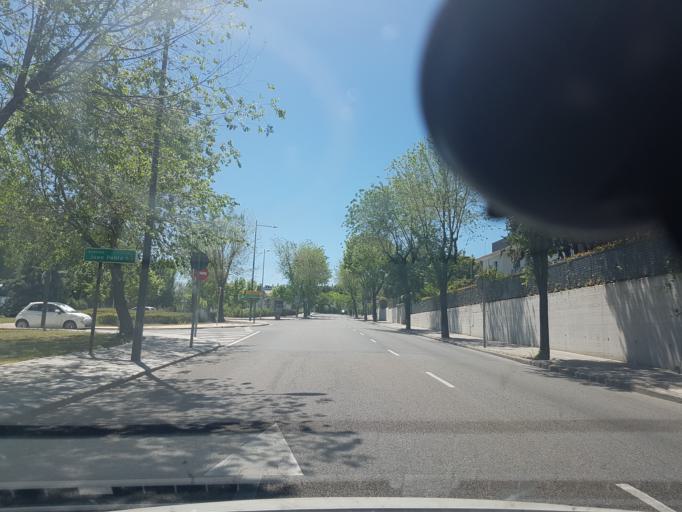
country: ES
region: Madrid
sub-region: Provincia de Madrid
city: Pozuelo de Alarcon
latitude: 40.4407
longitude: -3.8078
